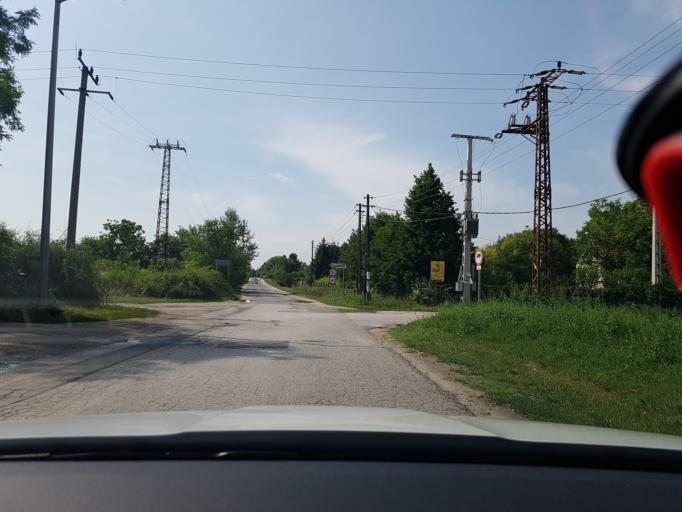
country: HU
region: Bacs-Kiskun
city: Kecskemet
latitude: 46.9202
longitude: 19.6532
